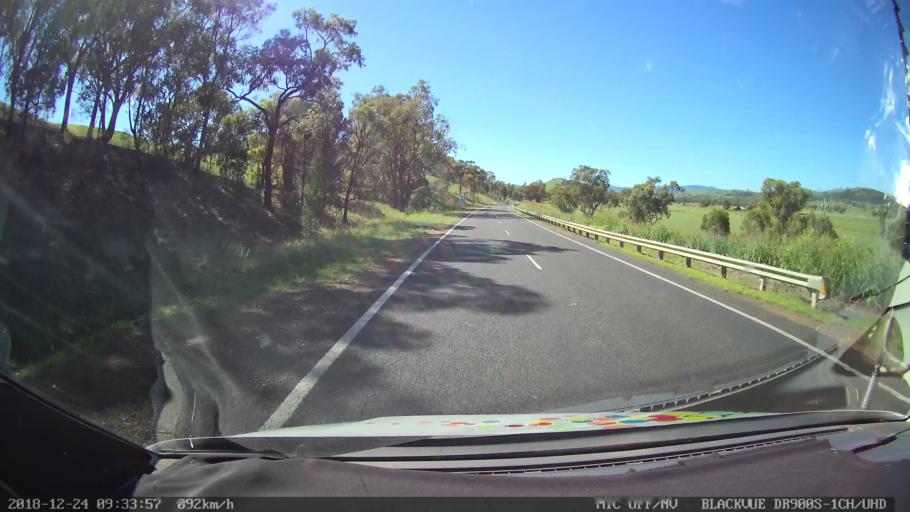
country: AU
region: New South Wales
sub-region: Liverpool Plains
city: Quirindi
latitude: -31.6087
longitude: 150.7125
